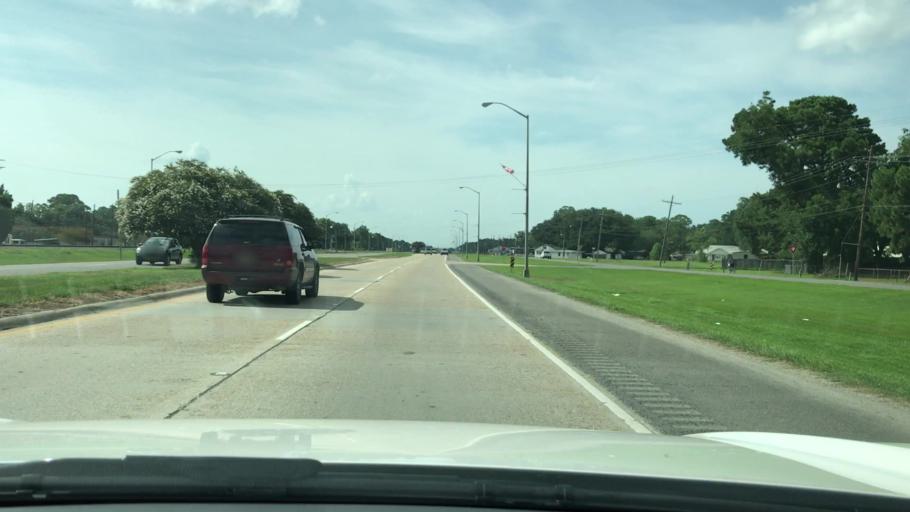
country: US
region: Louisiana
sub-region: Iberville Parish
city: Plaquemine
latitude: 30.3012
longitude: -91.2430
